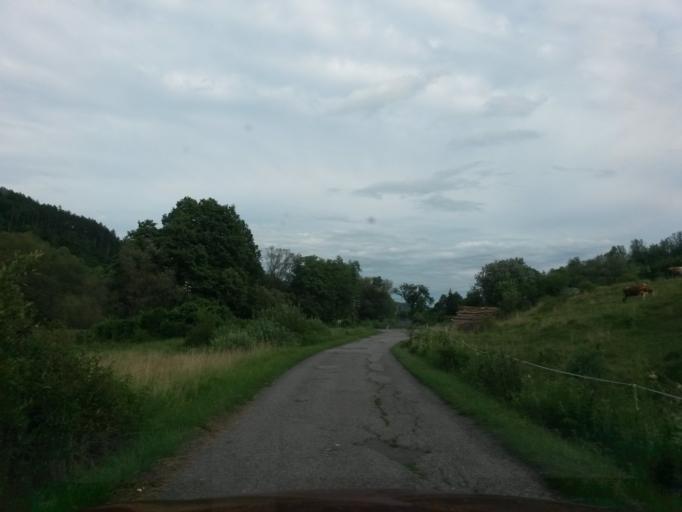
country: SK
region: Banskobystricky
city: Detva
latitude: 48.4345
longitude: 19.3474
